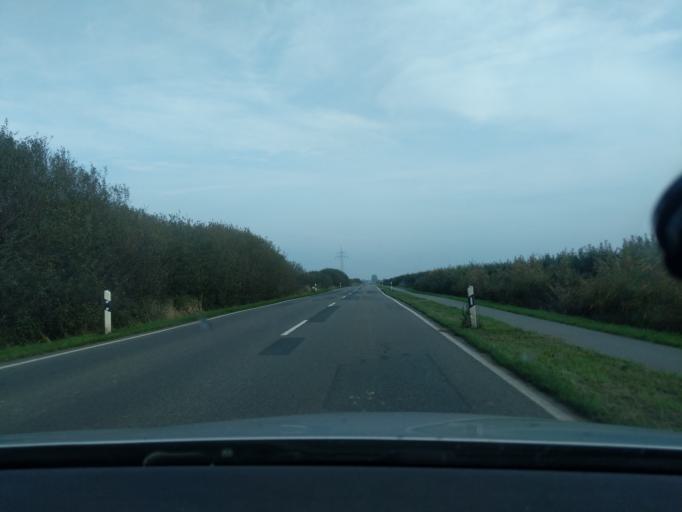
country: DE
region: Lower Saxony
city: Dollern
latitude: 53.5461
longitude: 9.5775
